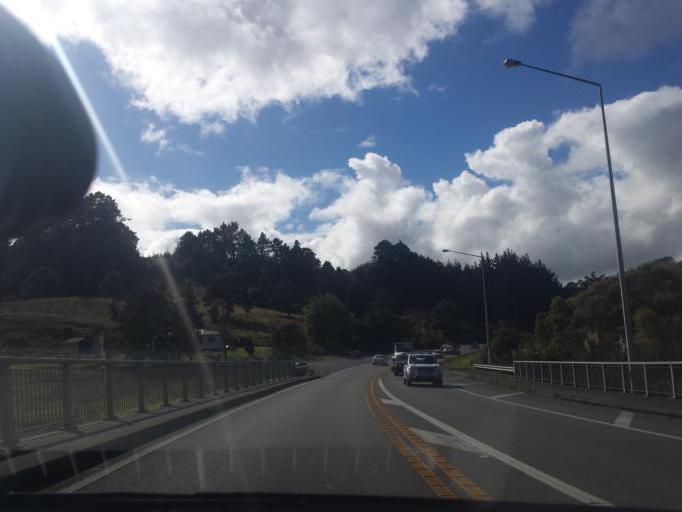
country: NZ
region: Auckland
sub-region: Auckland
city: Warkworth
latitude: -36.5151
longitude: 174.6691
